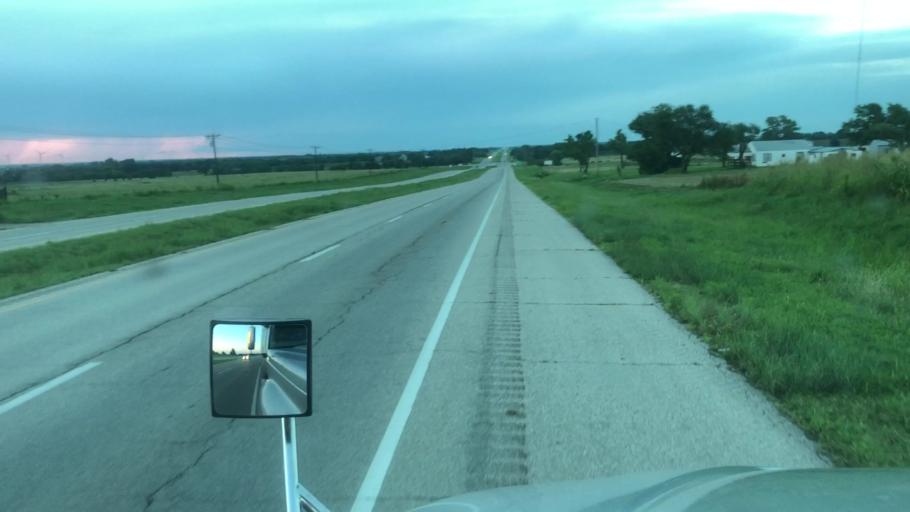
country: US
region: Oklahoma
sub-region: Kay County
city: Newkirk
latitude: 36.8030
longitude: -97.0672
